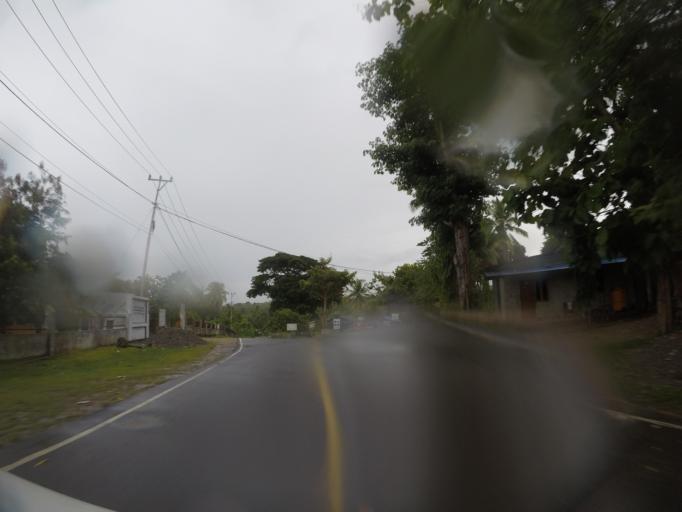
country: TL
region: Bobonaro
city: Maliana
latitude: -8.9688
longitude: 125.0451
